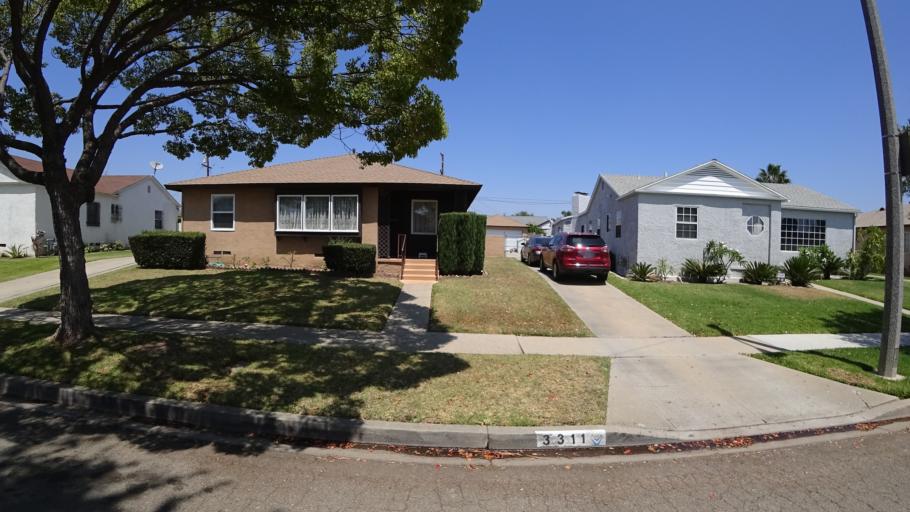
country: US
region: California
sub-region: Los Angeles County
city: Lennox
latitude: 33.9292
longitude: -118.3293
